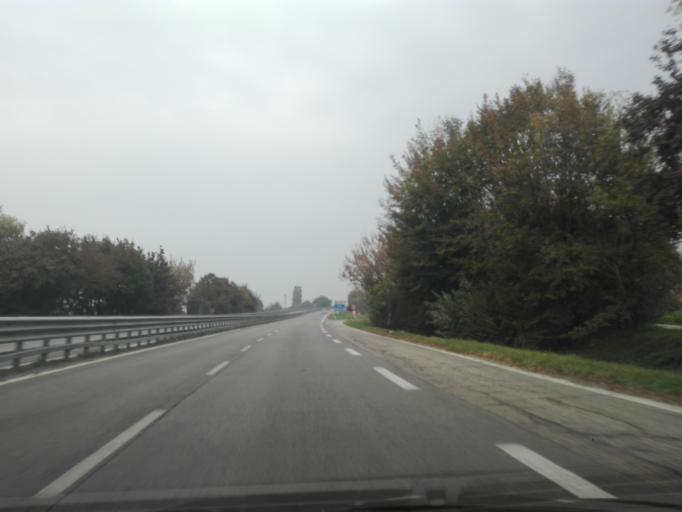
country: IT
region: Veneto
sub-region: Provincia di Verona
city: Villa Bartolomea
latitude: 45.1629
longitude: 11.3054
